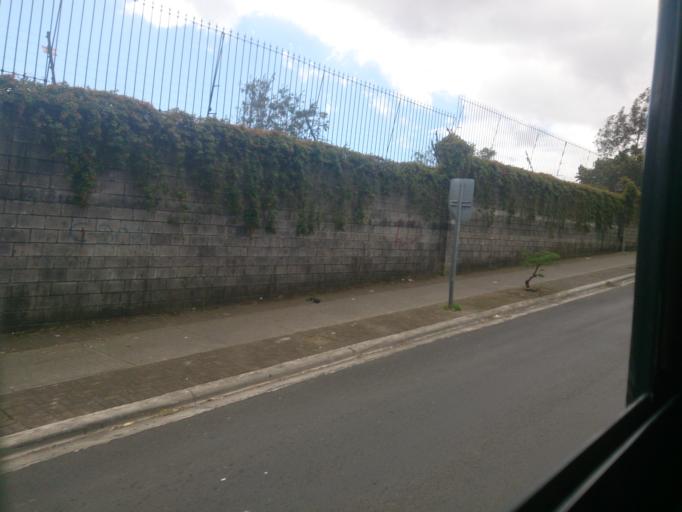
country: CR
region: Cartago
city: Concepcion
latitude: 9.9291
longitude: -84.0085
